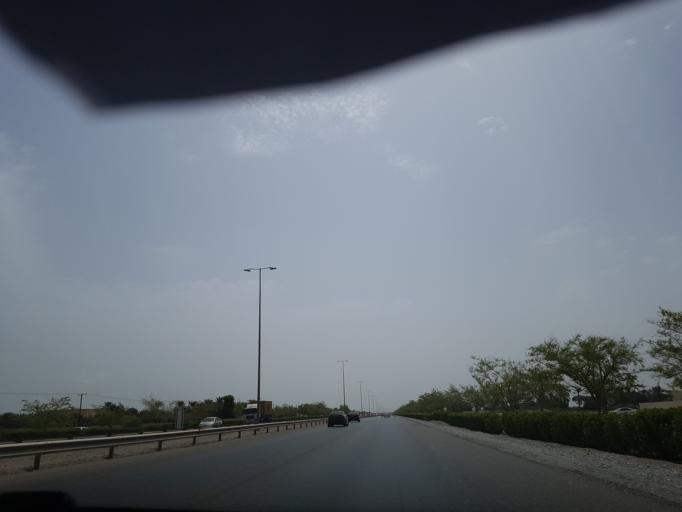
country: OM
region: Al Batinah
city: Barka'
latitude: 23.7324
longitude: 57.6921
